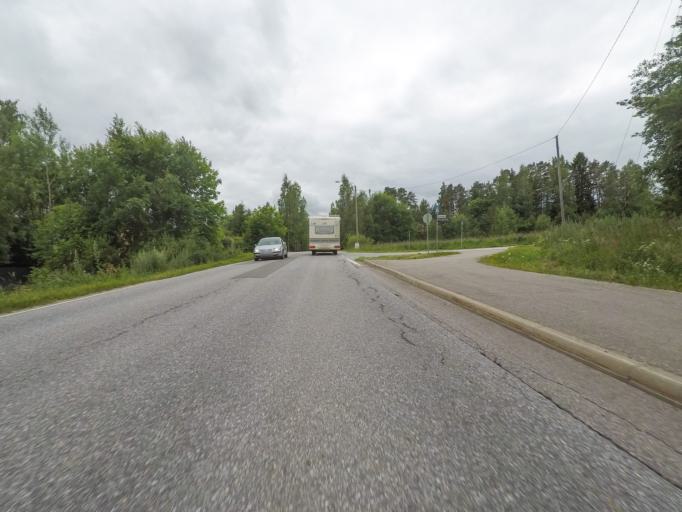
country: FI
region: Varsinais-Suomi
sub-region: Salo
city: Muurla
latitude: 60.3613
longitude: 23.2960
